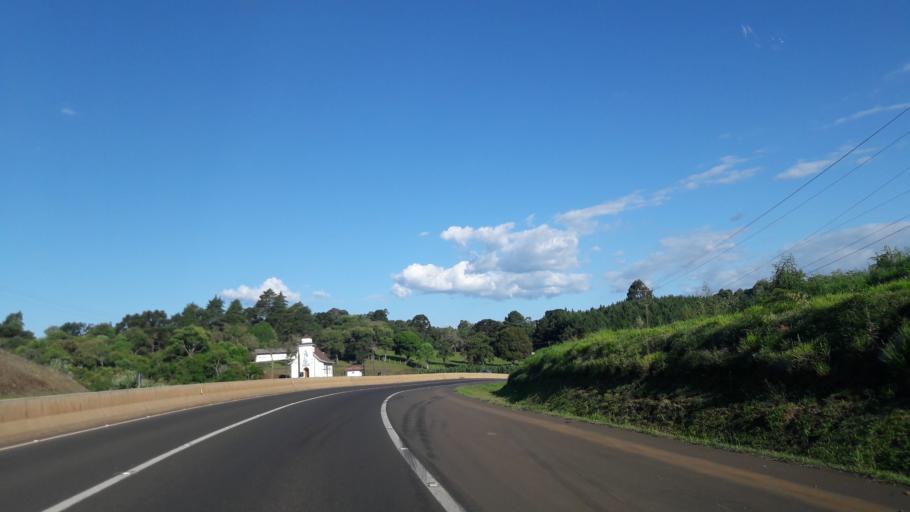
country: BR
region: Parana
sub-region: Guarapuava
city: Guarapuava
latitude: -25.3443
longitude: -51.3936
